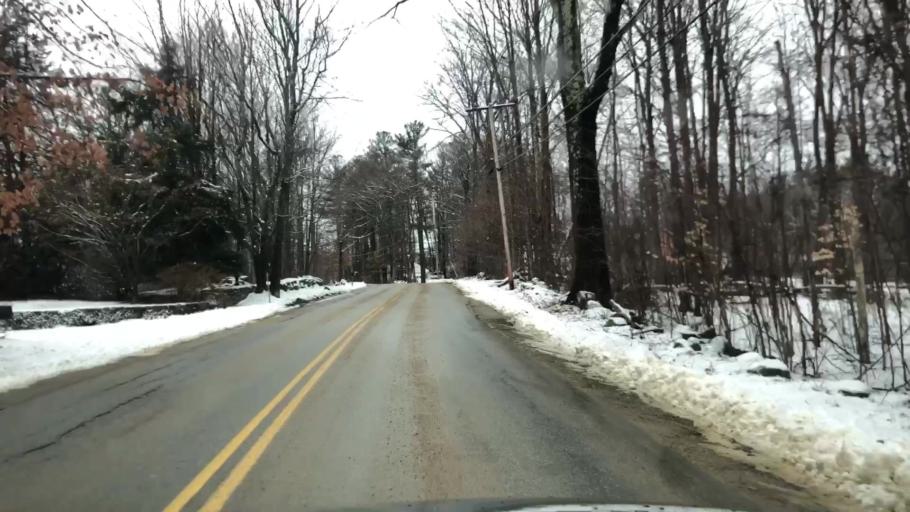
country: US
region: New Hampshire
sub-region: Hillsborough County
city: Mont Vernon
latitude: 42.9211
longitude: -71.6006
